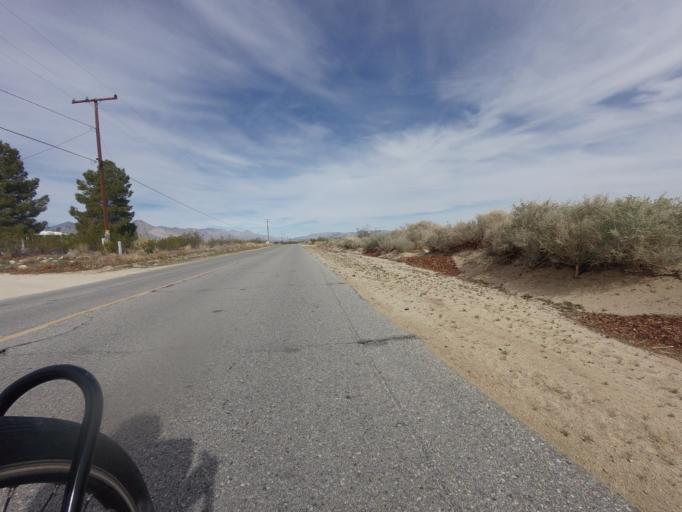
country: US
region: California
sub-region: Kern County
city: Inyokern
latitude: 35.7051
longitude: -117.8296
